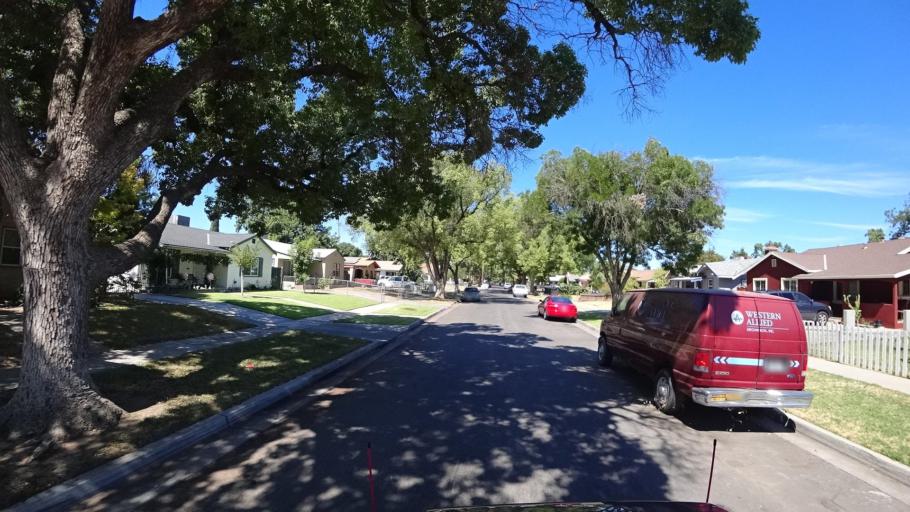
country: US
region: California
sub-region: Fresno County
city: Fresno
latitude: 36.7459
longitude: -119.7481
